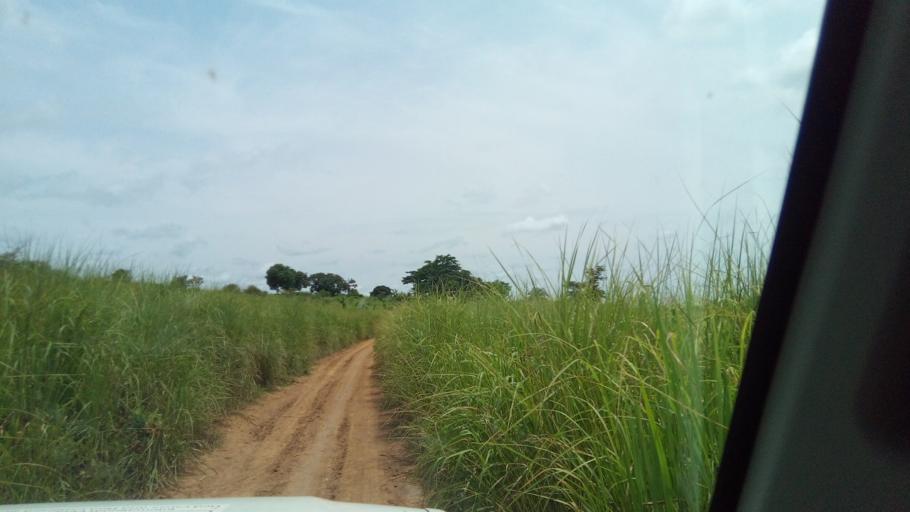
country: AO
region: Zaire
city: Mbanza Congo
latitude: -5.7995
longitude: 13.9960
